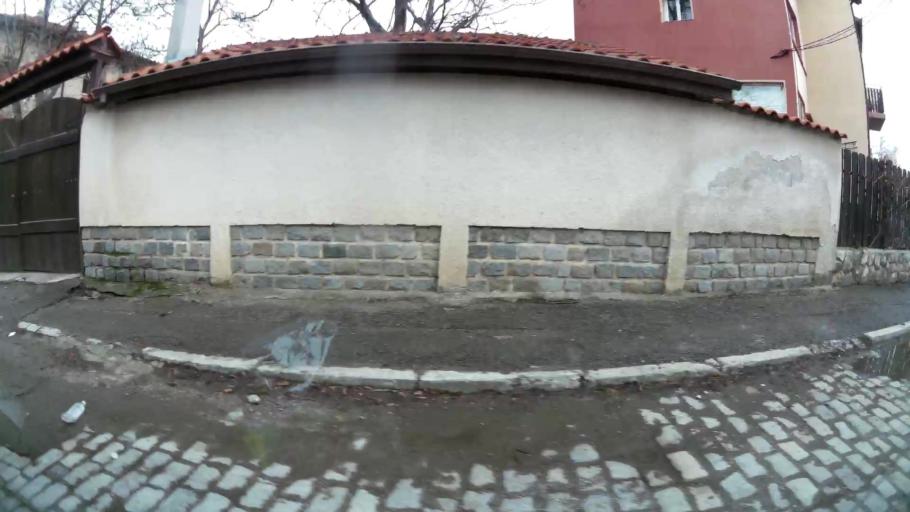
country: BG
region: Sofiya
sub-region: Obshtina Bozhurishte
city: Bozhurishte
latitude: 42.7429
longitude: 23.2662
